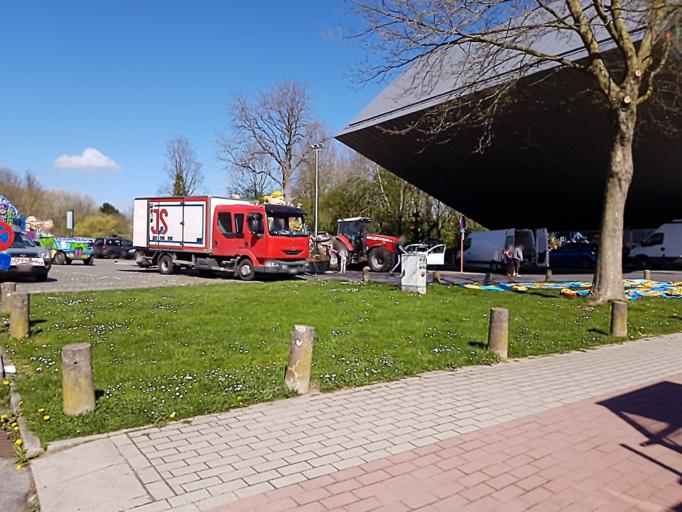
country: BE
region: Flanders
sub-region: Provincie Vlaams-Brabant
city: Dilbeek
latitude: 50.8499
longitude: 4.2621
